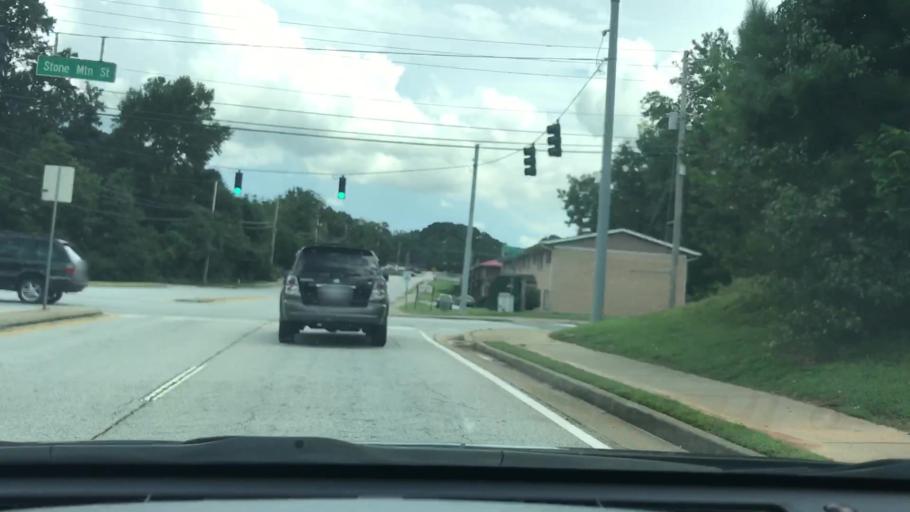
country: US
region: Georgia
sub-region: Gwinnett County
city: Lawrenceville
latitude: 33.9465
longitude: -83.9920
